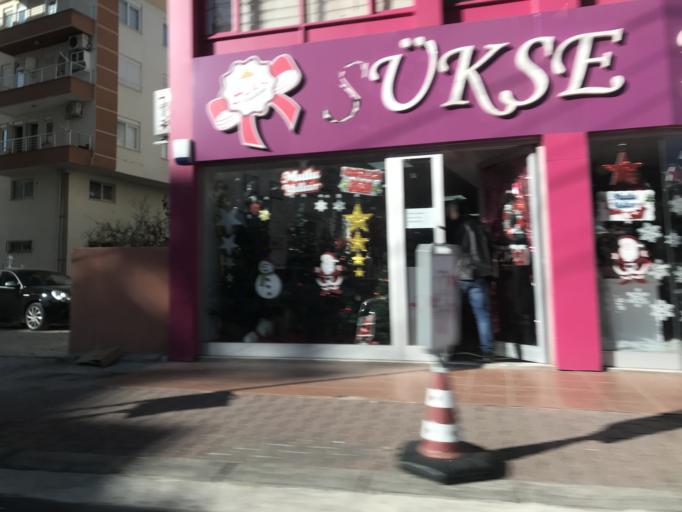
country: TR
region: Antalya
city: Antalya
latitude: 36.8988
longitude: 30.7076
